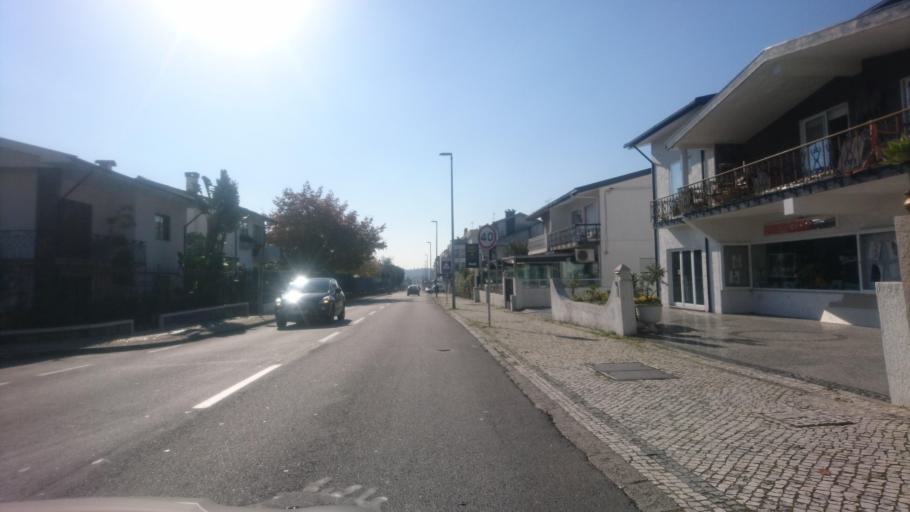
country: PT
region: Aveiro
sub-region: Santa Maria da Feira
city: Feira
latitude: 40.9254
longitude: -8.5582
